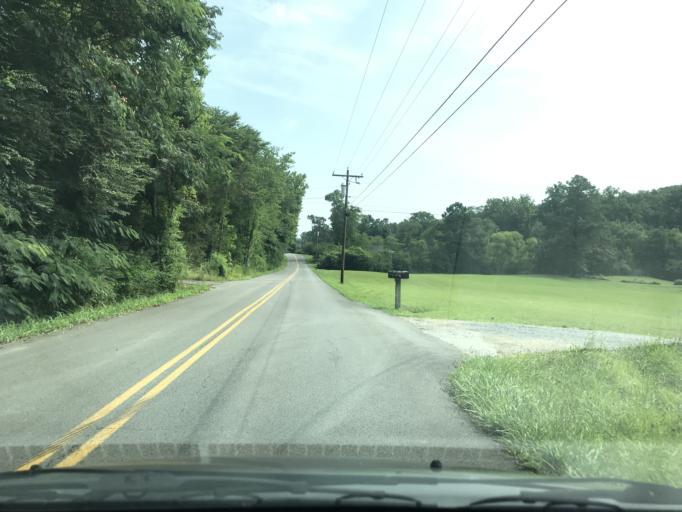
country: US
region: Tennessee
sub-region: Hamilton County
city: Apison
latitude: 35.0777
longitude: -84.9746
